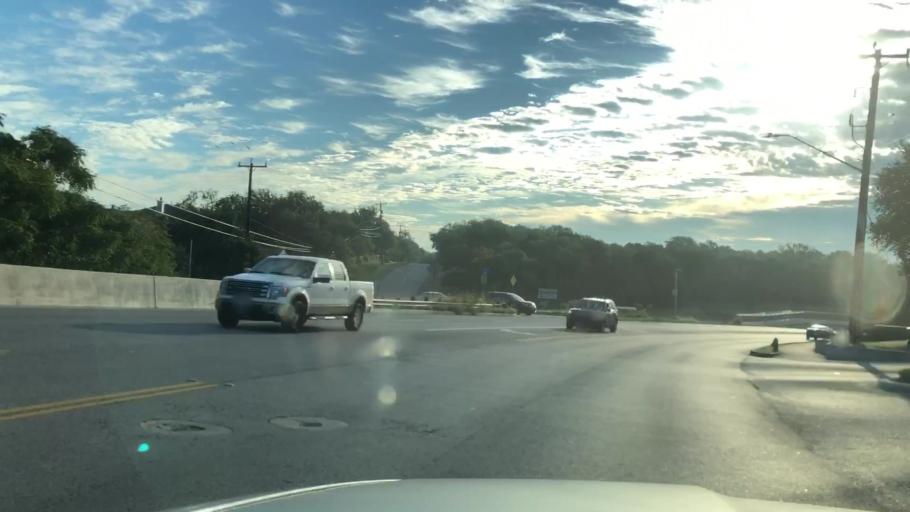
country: US
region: Texas
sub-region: Bexar County
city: Leon Valley
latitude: 29.5444
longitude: -98.6388
